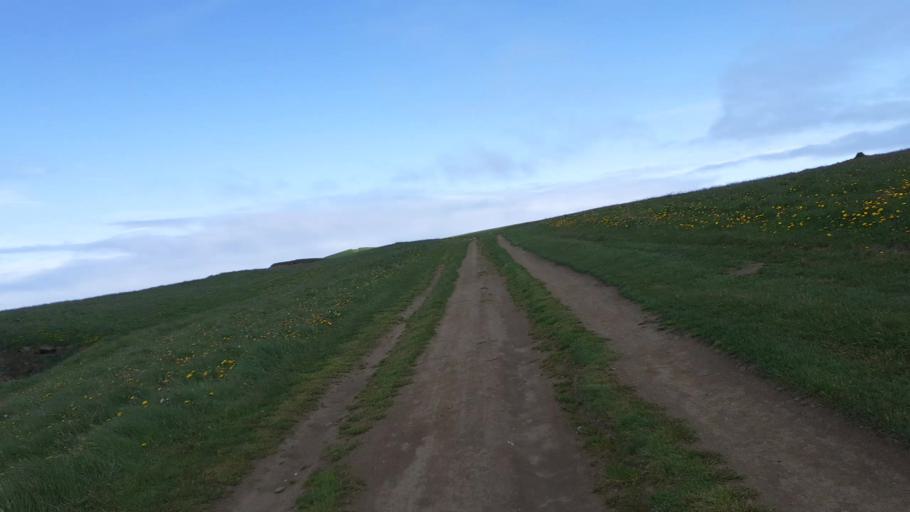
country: IS
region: Northeast
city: Dalvik
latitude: 66.5543
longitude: -18.0124
